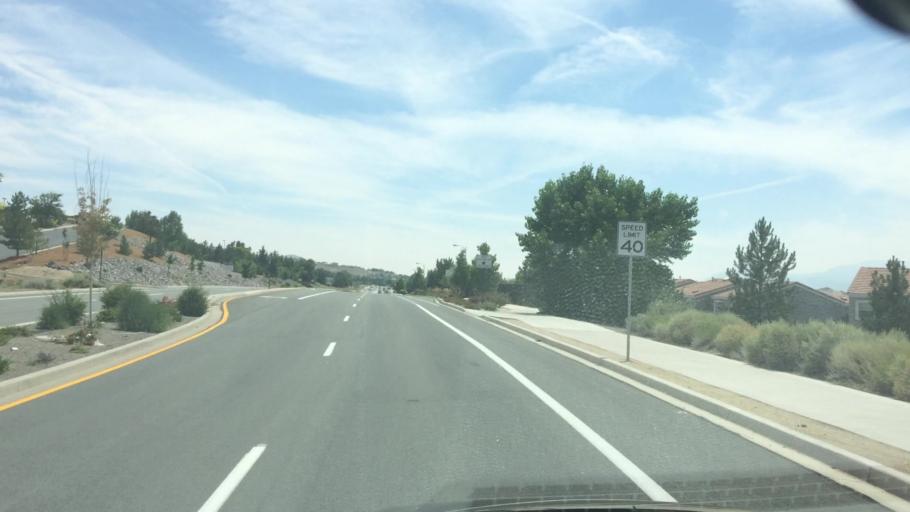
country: US
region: Nevada
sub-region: Washoe County
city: Spanish Springs
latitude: 39.5957
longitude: -119.7147
